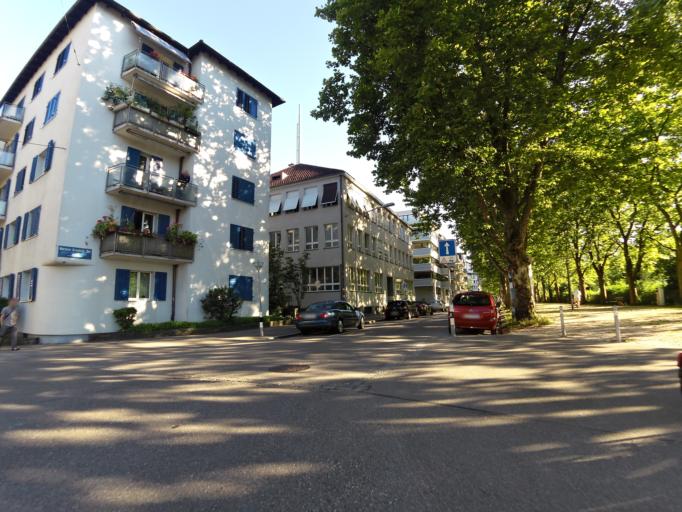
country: CH
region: Zurich
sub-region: Bezirk Zuerich
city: Aussersihl
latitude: 47.3797
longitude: 8.5214
